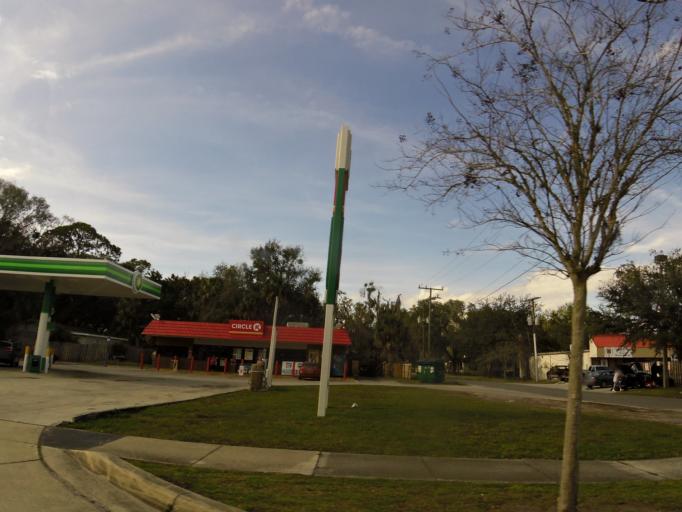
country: US
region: Florida
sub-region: Flagler County
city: Bunnell
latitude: 29.4685
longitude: -81.2552
